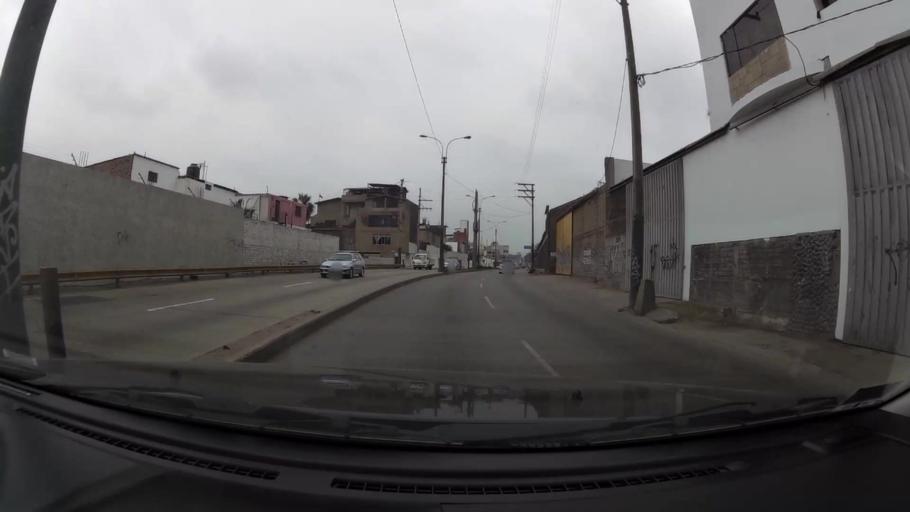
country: PE
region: Lima
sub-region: Lima
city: Surco
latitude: -12.1344
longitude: -76.9765
